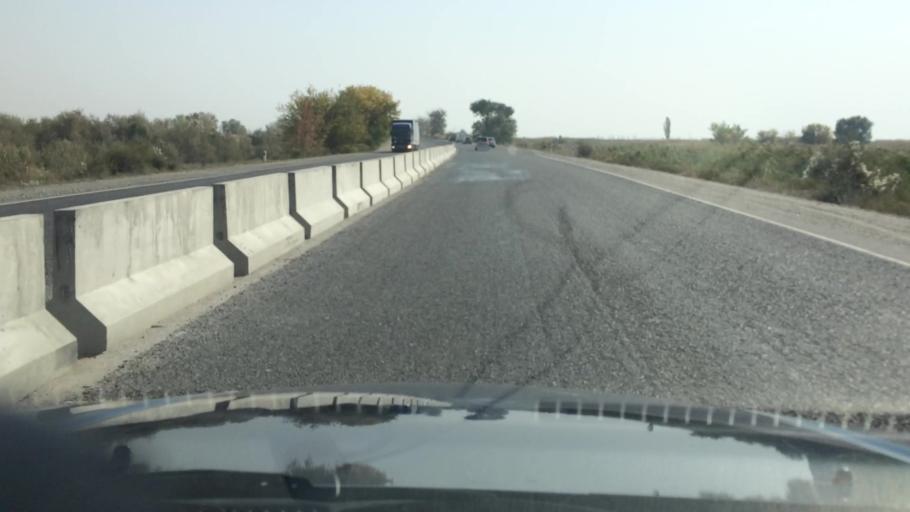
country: KG
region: Chuy
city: Kant
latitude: 42.9597
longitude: 74.9232
